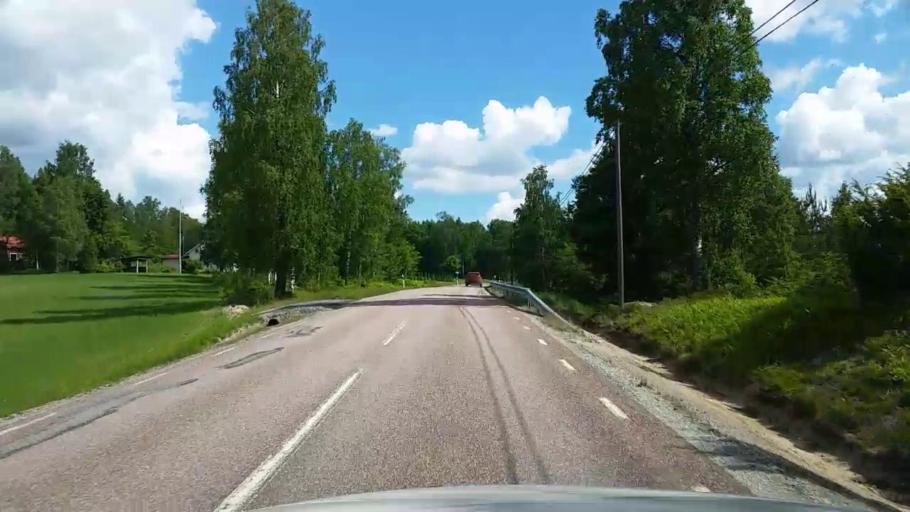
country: SE
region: Vaestmanland
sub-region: Skinnskattebergs Kommun
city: Skinnskatteberg
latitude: 59.7641
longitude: 15.8267
